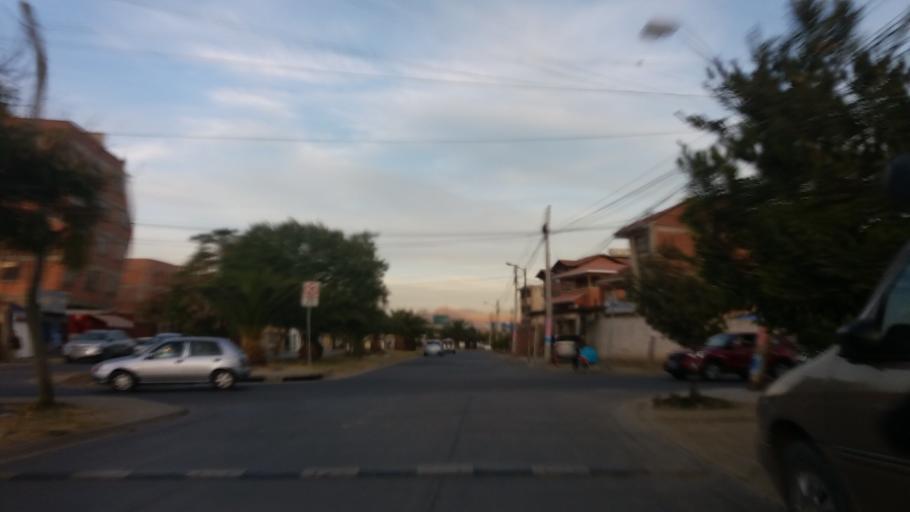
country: BO
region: Cochabamba
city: Cochabamba
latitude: -17.3774
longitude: -66.1909
